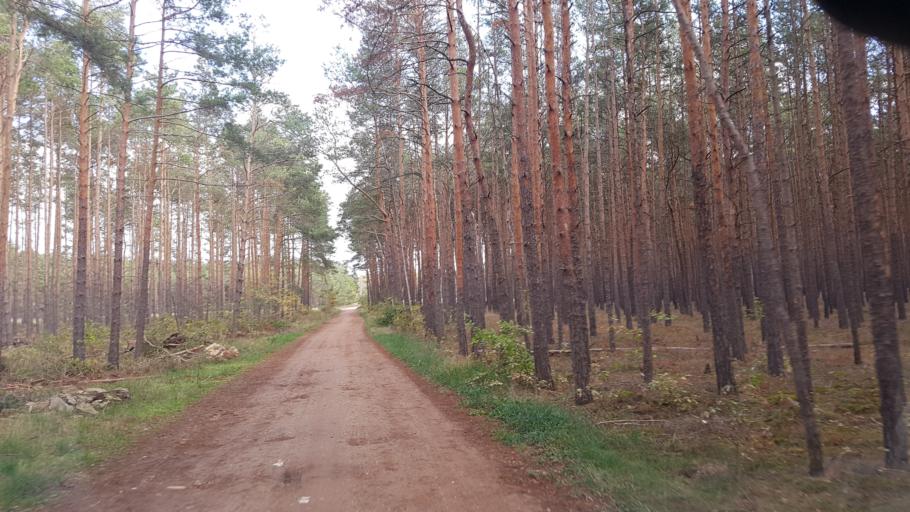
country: DE
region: Brandenburg
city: Sonnewalde
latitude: 51.6572
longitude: 13.6502
